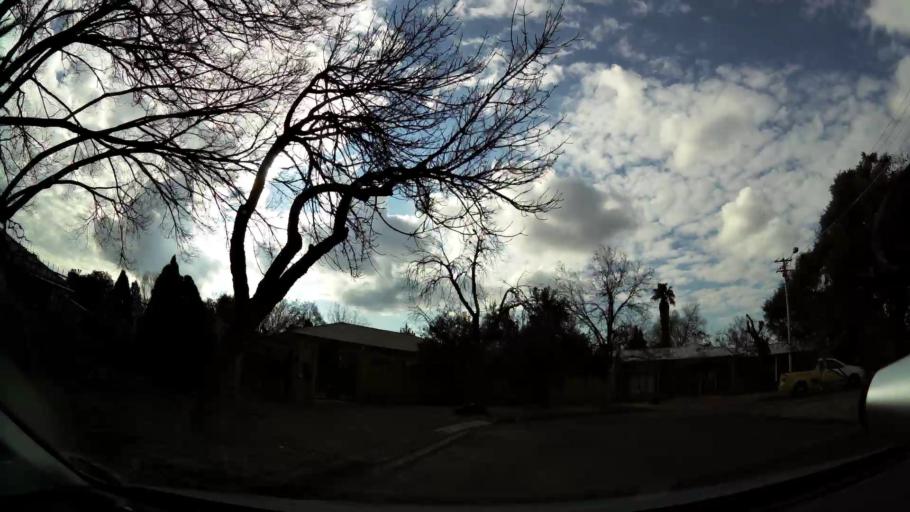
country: ZA
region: Orange Free State
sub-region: Mangaung Metropolitan Municipality
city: Bloemfontein
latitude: -29.0819
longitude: 26.2077
